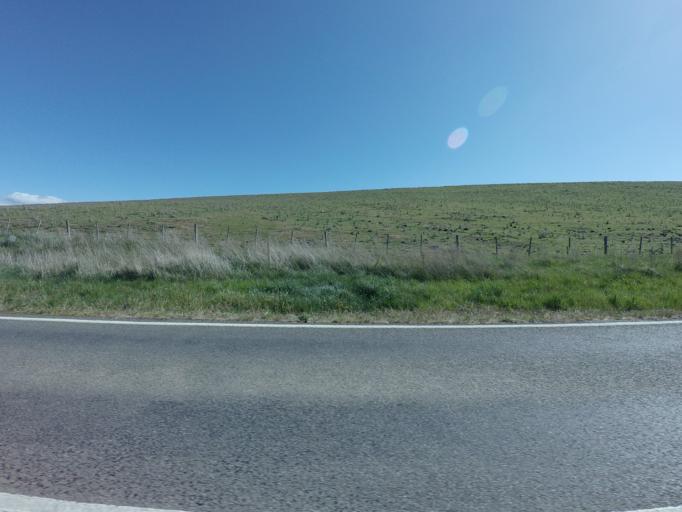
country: AU
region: Tasmania
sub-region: Derwent Valley
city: New Norfolk
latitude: -42.6394
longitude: 146.9184
